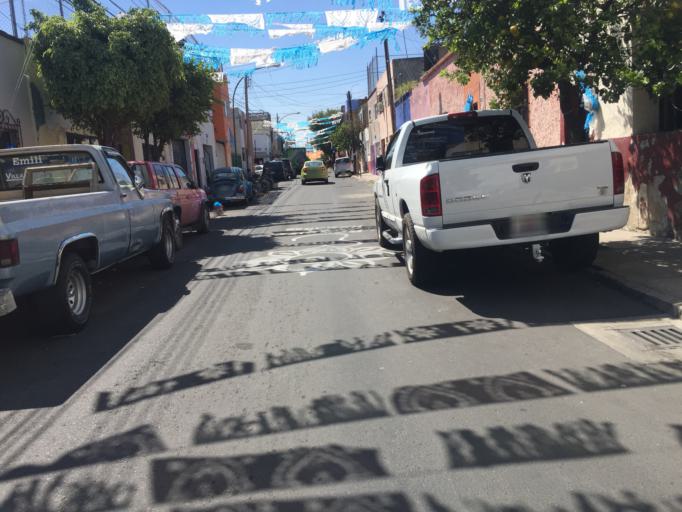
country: MX
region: Jalisco
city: Guadalajara
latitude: 20.6869
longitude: -103.3622
